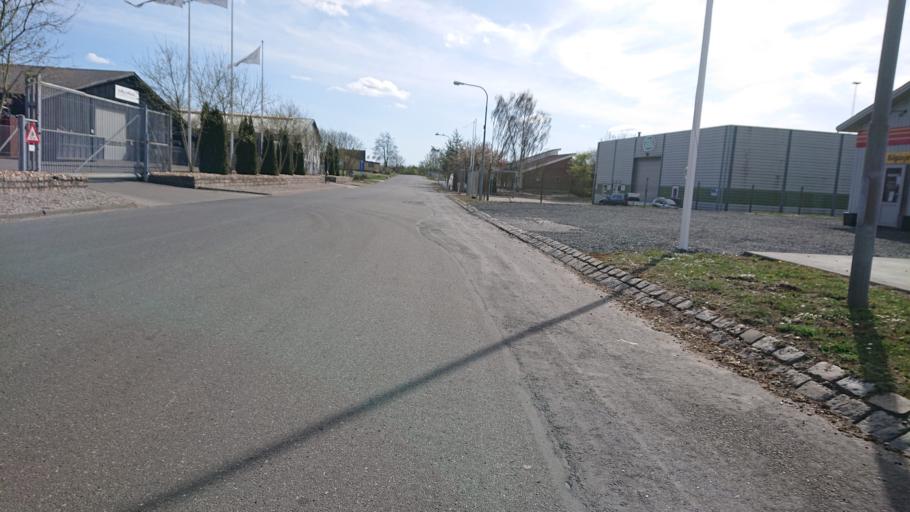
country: DK
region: South Denmark
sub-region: Nyborg Kommune
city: Nyborg
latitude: 55.3128
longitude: 10.7522
